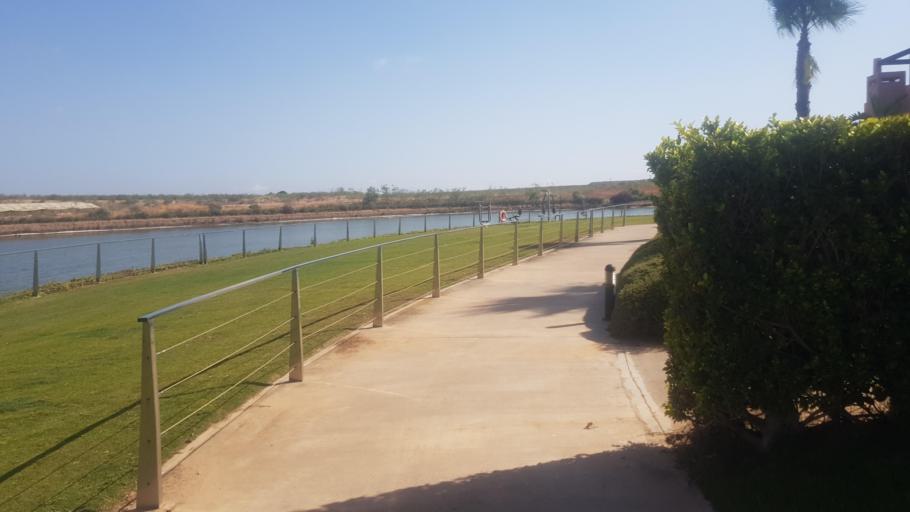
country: ES
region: Murcia
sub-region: Murcia
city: Mazarron
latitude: 37.7307
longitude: -1.3445
